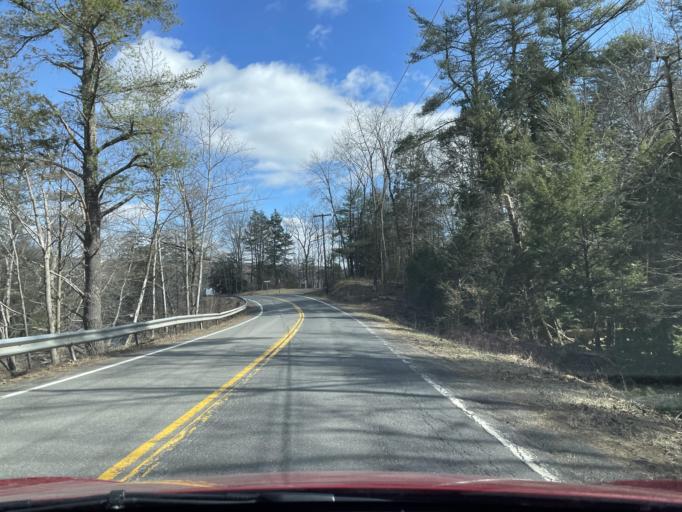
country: US
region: New York
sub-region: Ulster County
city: Zena
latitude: 42.0011
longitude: -74.0551
